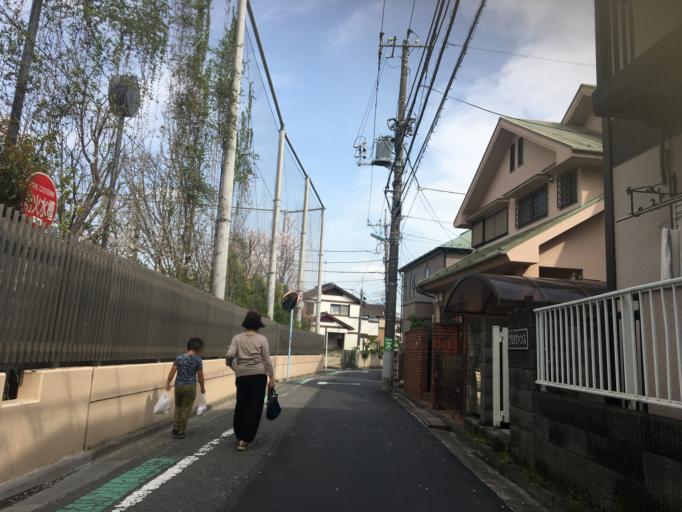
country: JP
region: Tokyo
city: Musashino
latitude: 35.7104
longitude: 139.6232
